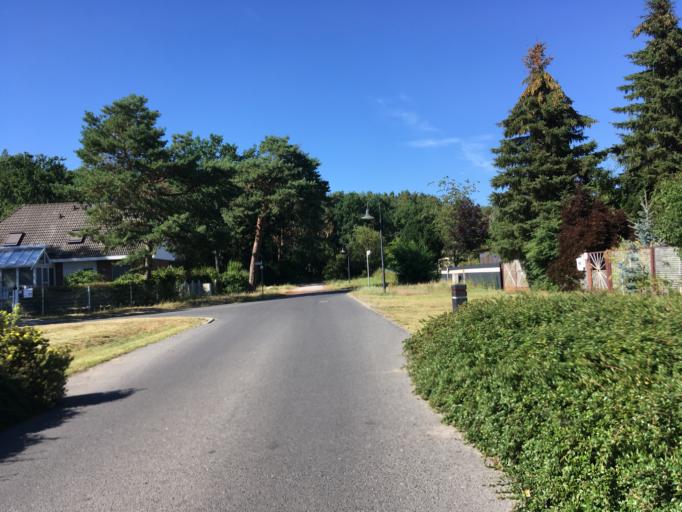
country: DE
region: Brandenburg
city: Schulzendorf
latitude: 52.3750
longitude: 13.5930
